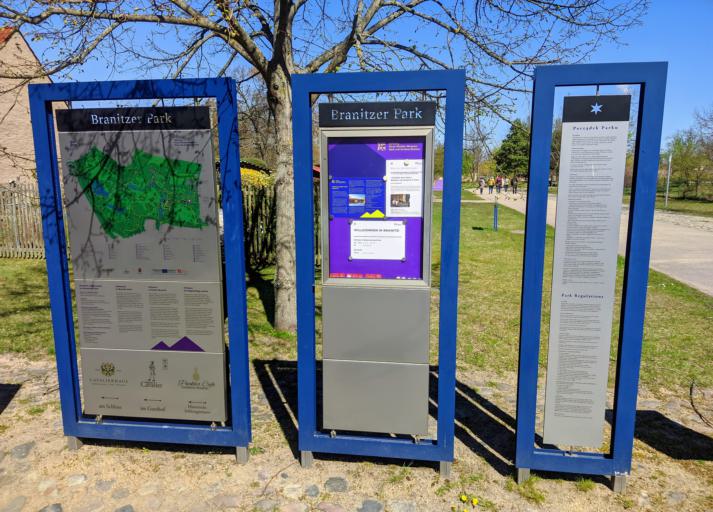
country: DE
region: Brandenburg
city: Cottbus
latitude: 51.7422
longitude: 14.3737
